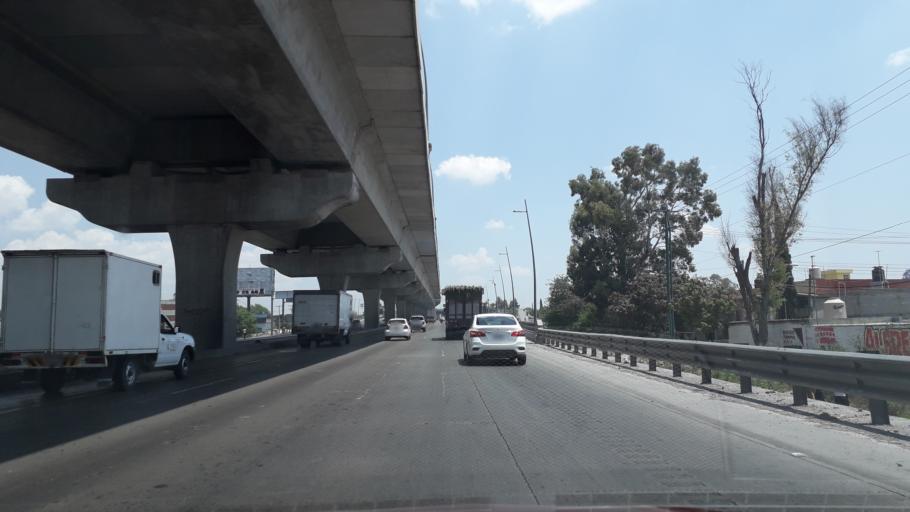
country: MX
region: Puebla
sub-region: Cuautlancingo
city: Sanctorum
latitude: 19.0935
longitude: -98.2245
